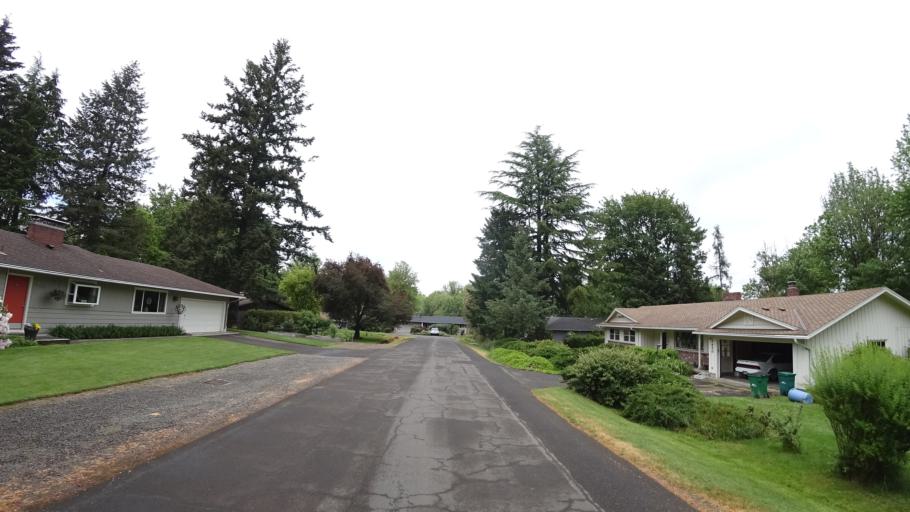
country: US
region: Oregon
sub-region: Washington County
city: Garden Home-Whitford
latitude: 45.4662
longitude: -122.7726
